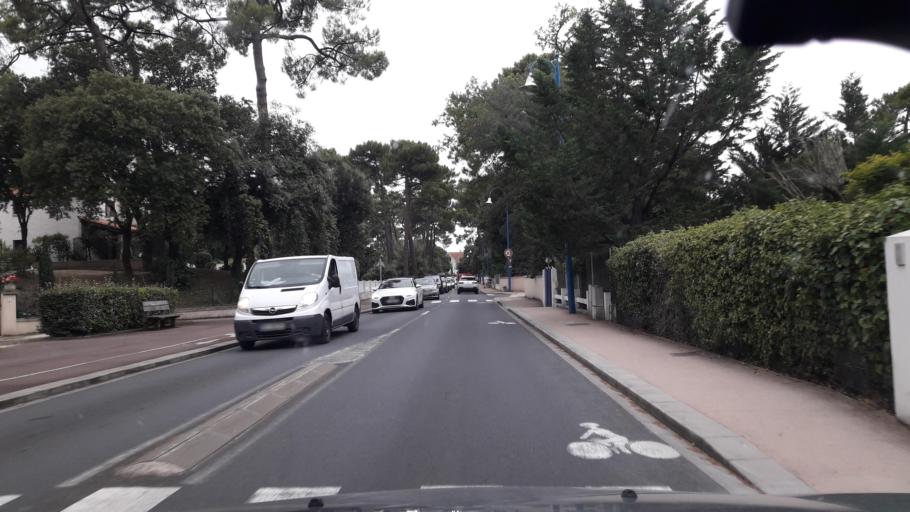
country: FR
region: Poitou-Charentes
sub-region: Departement de la Charente-Maritime
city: Les Mathes
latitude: 45.6940
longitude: -1.1777
